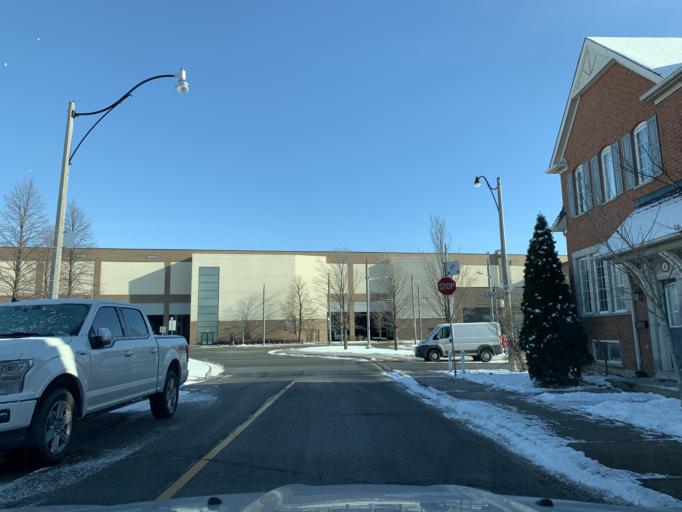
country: CA
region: Ontario
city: Toronto
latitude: 43.6722
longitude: -79.4725
